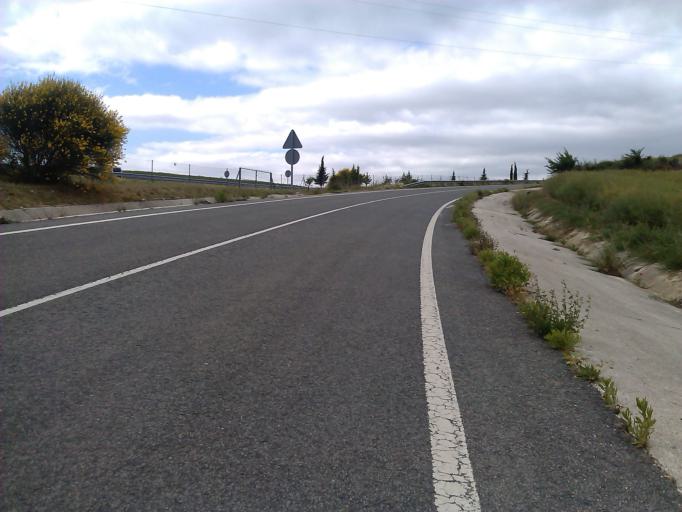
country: ES
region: Navarre
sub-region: Provincia de Navarra
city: Puente la Reina
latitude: 42.6697
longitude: -1.8303
